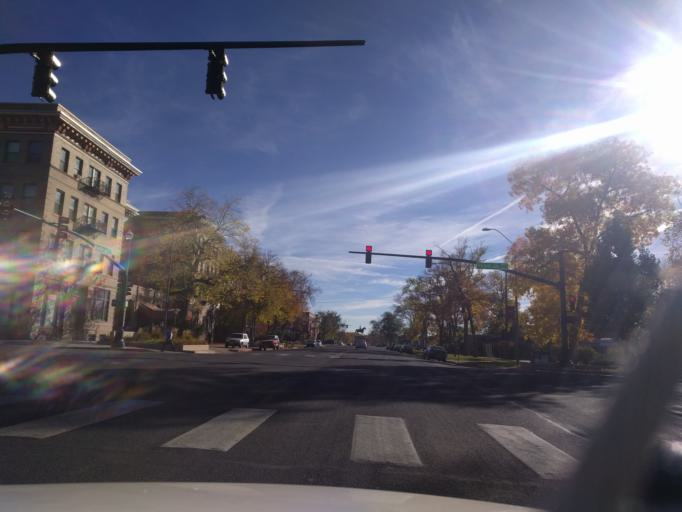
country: US
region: Colorado
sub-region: El Paso County
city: Colorado Springs
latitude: 38.8381
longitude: -104.8236
